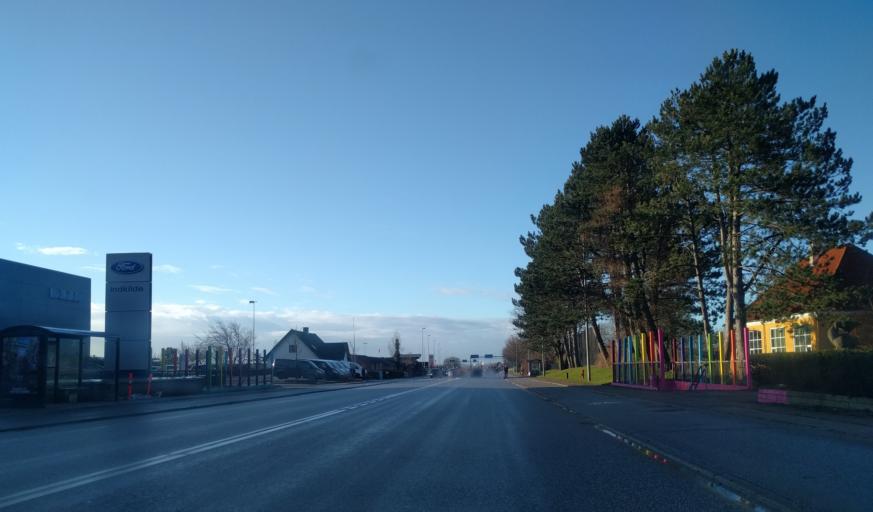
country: DK
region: North Denmark
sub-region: Alborg Kommune
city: Aalborg
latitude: 57.0167
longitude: 9.8957
